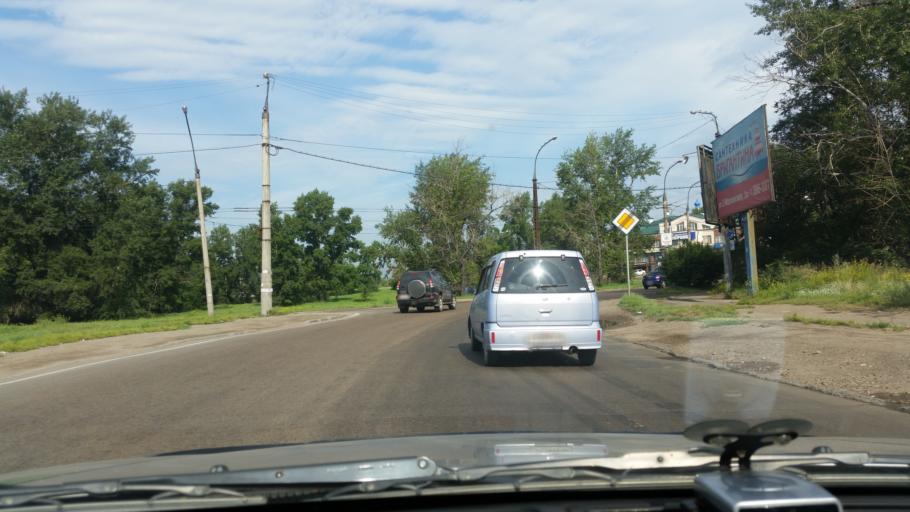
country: RU
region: Irkutsk
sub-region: Irkutskiy Rayon
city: Irkutsk
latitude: 52.2984
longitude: 104.2986
